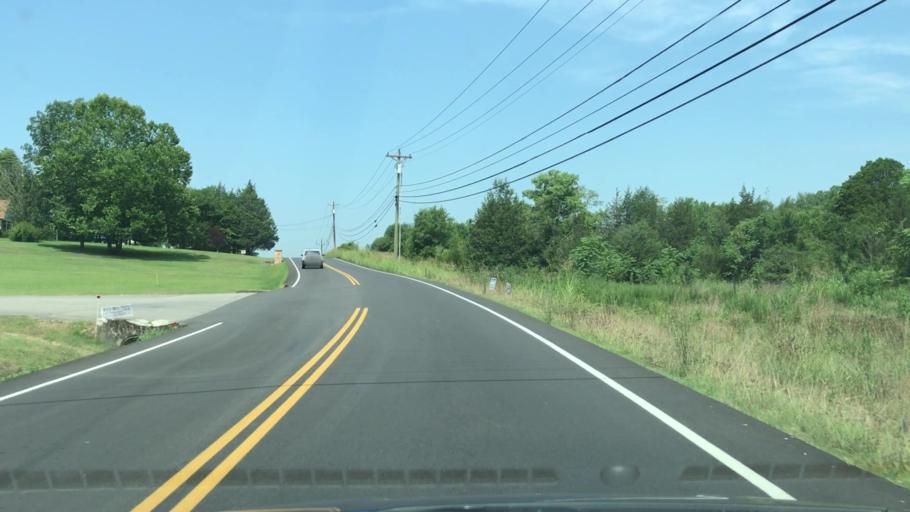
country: US
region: Tennessee
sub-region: Wilson County
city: Rural Hill
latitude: 36.1254
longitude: -86.5148
